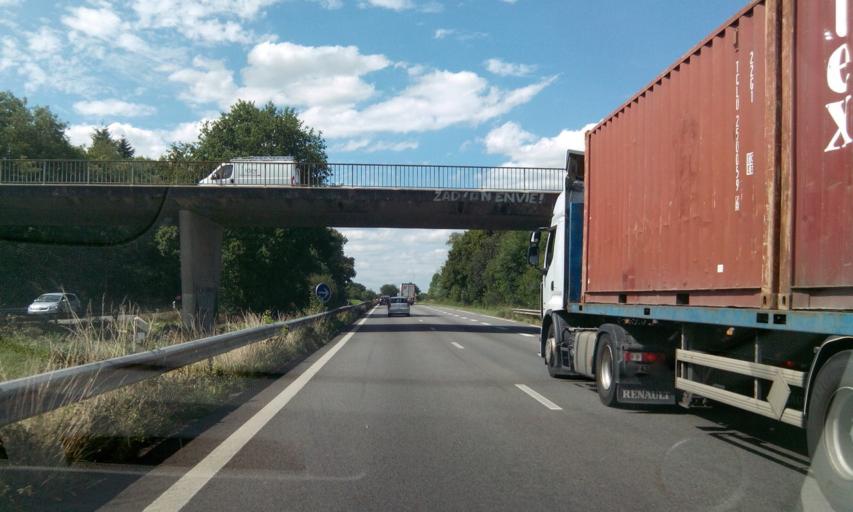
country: FR
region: Pays de la Loire
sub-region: Departement de la Loire-Atlantique
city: Vigneux-de-Bretagne
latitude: 47.3004
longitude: -1.7540
